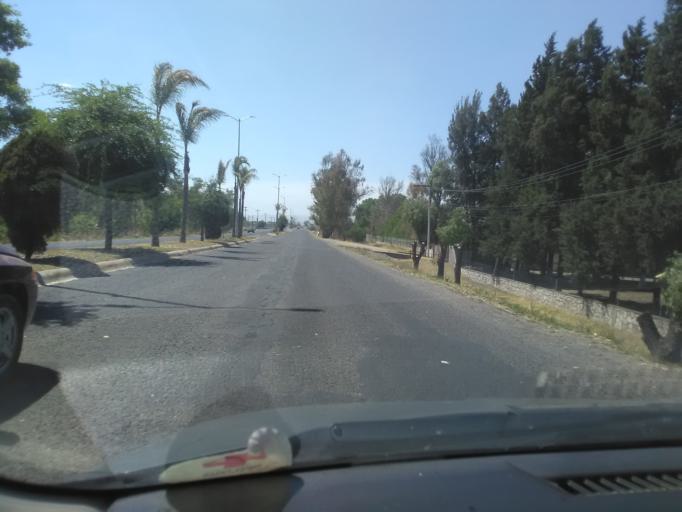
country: MX
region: Durango
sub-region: Durango
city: Jose Refugio Salcido
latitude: 24.0255
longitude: -104.5662
